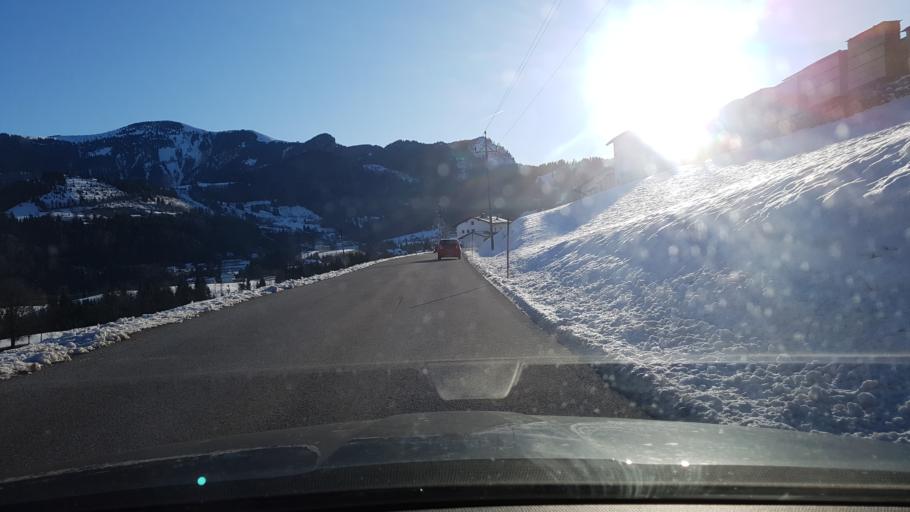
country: AT
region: Salzburg
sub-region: Politischer Bezirk Hallein
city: Kuchl
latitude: 47.6535
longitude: 13.2039
